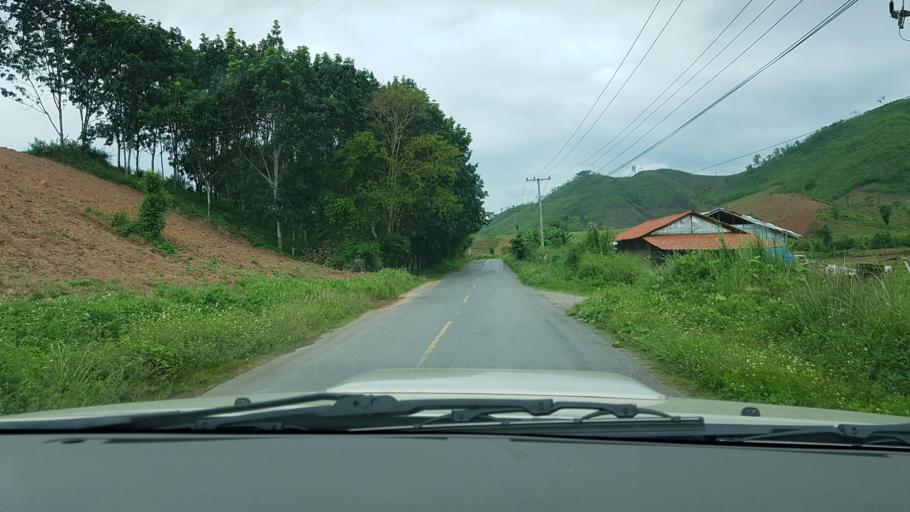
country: LA
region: Loungnamtha
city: Muang Nale
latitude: 20.3748
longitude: 101.7267
